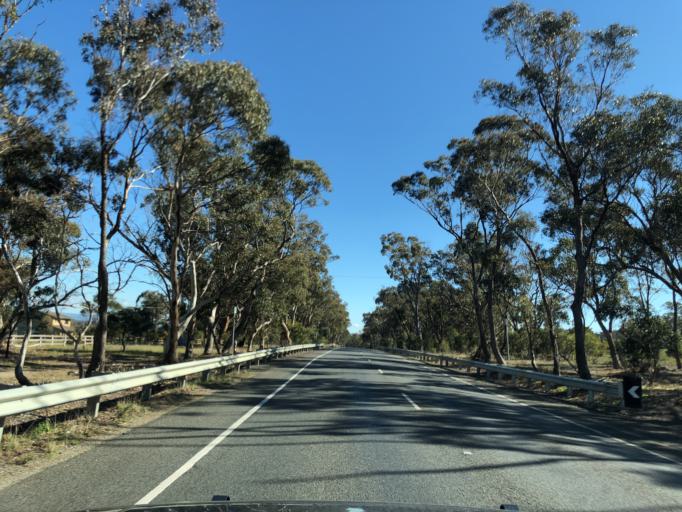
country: AU
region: Victoria
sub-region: Melton
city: Melton West
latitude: -37.6131
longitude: 144.5602
